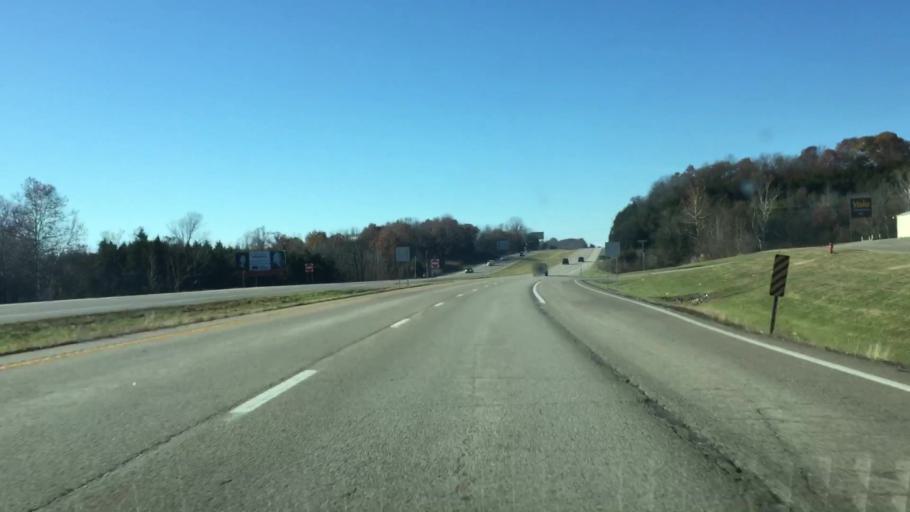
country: US
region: Missouri
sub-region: Cole County
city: Wardsville
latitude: 38.5279
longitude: -92.2221
